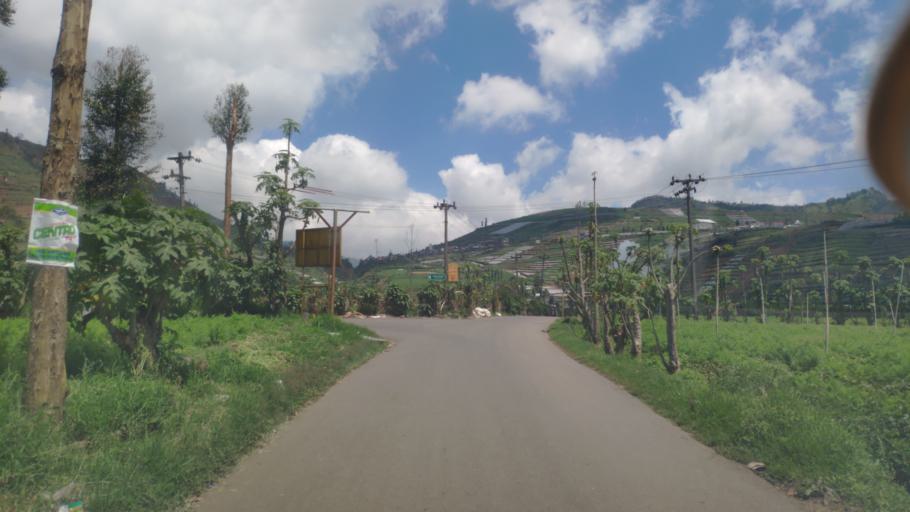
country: ID
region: Central Java
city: Wonosobo
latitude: -7.1994
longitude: 109.8805
